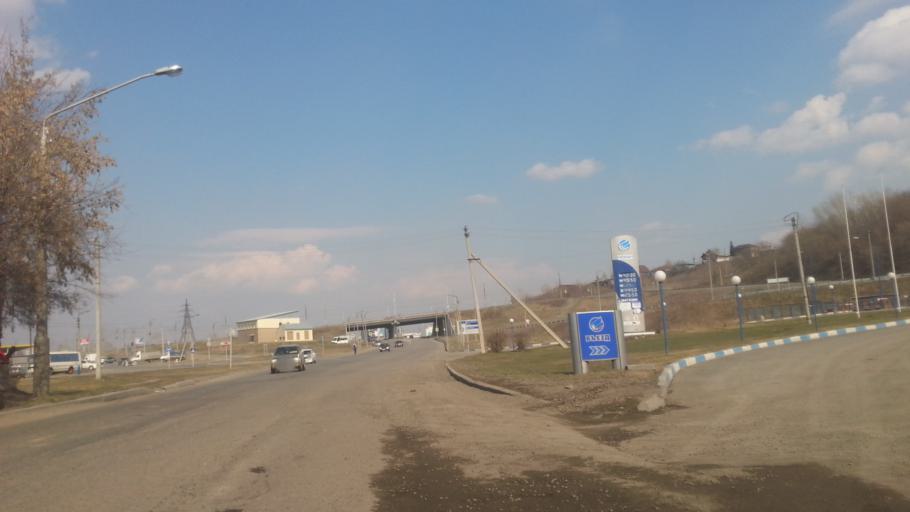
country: RU
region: Altai Krai
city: Zaton
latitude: 53.3217
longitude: 83.7829
